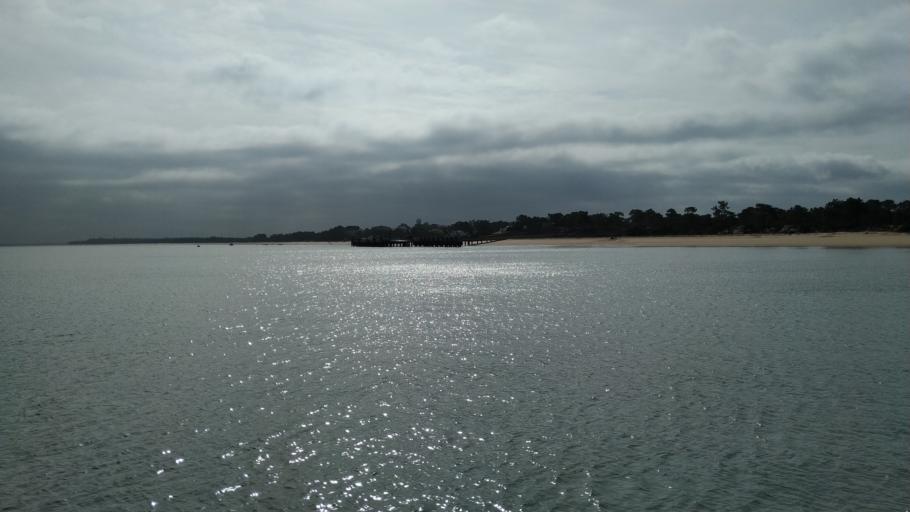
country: PT
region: Setubal
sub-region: Setubal
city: Setubal
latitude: 38.4709
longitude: -8.8653
